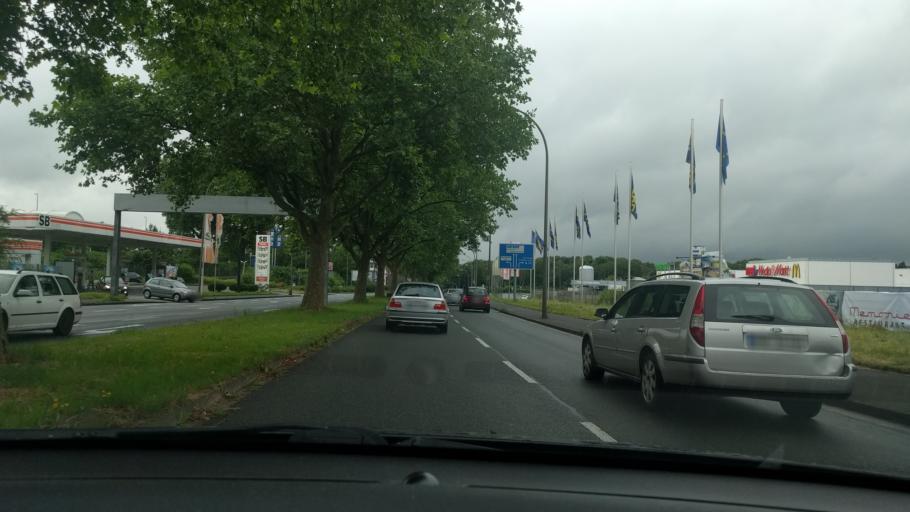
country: DE
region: North Rhine-Westphalia
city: Witten
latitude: 51.4922
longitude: 7.3710
